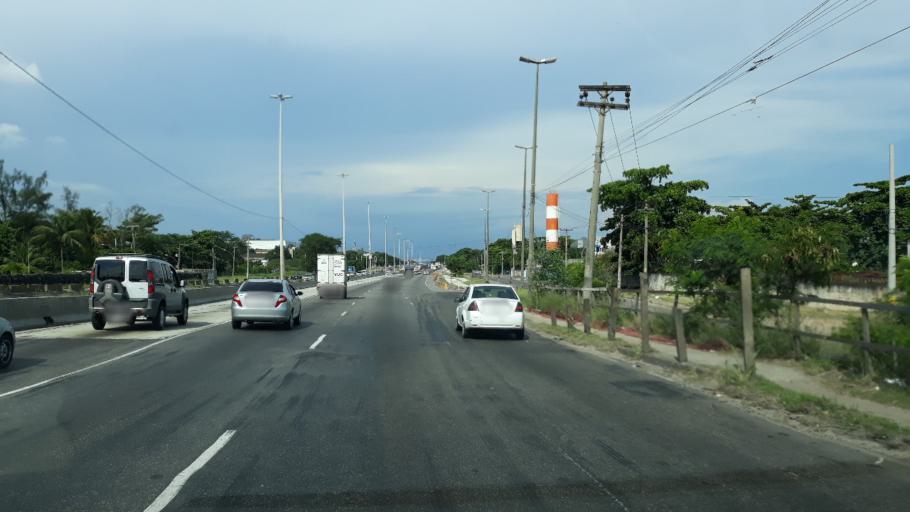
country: BR
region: Rio de Janeiro
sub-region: Sao Joao De Meriti
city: Sao Joao de Meriti
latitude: -22.8345
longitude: -43.3595
